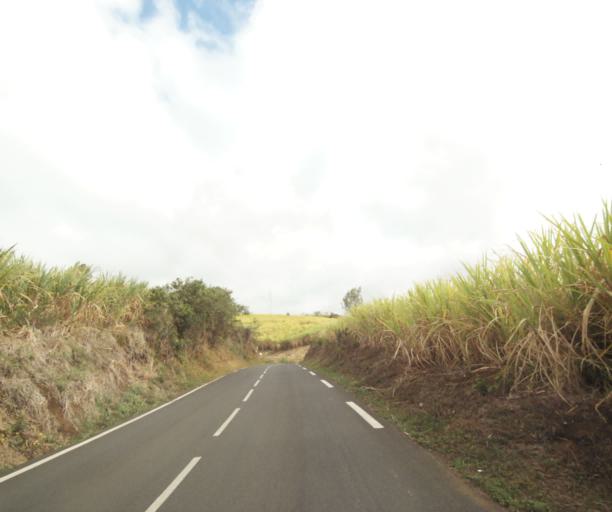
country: RE
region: Reunion
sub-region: Reunion
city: Saint-Paul
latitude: -21.0251
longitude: 55.3141
